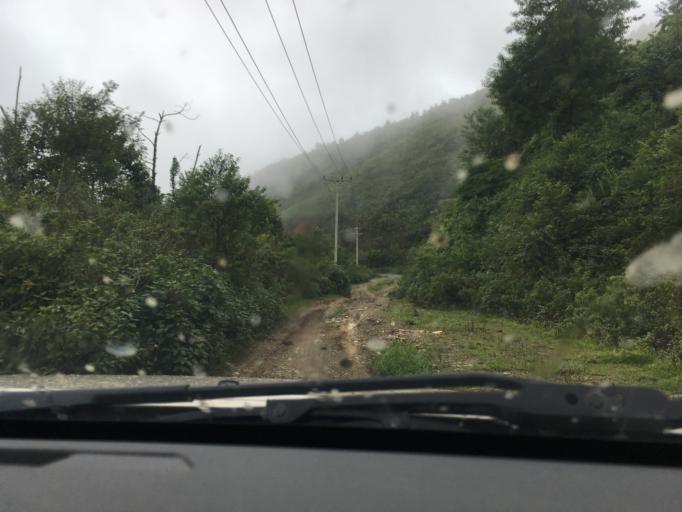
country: LA
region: Phongsali
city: Phongsali
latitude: 21.3921
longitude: 102.2050
